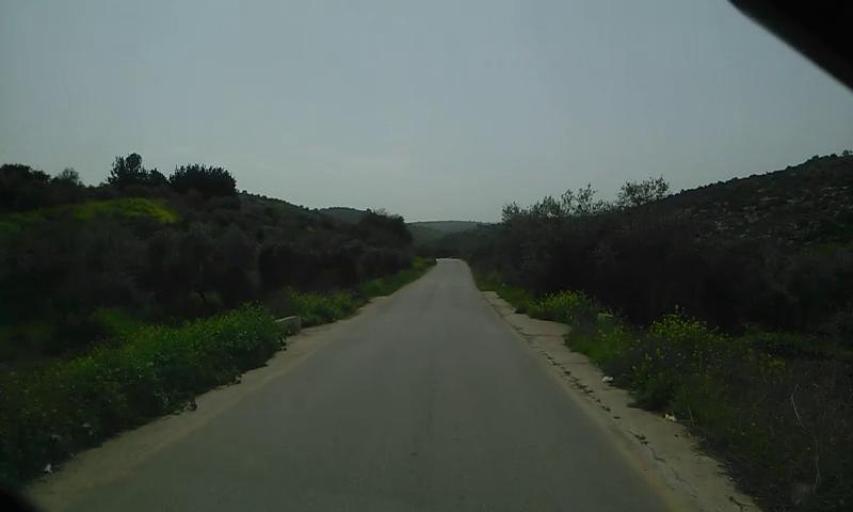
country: PS
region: West Bank
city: Silat al Harithiyah
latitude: 32.5156
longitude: 35.2157
